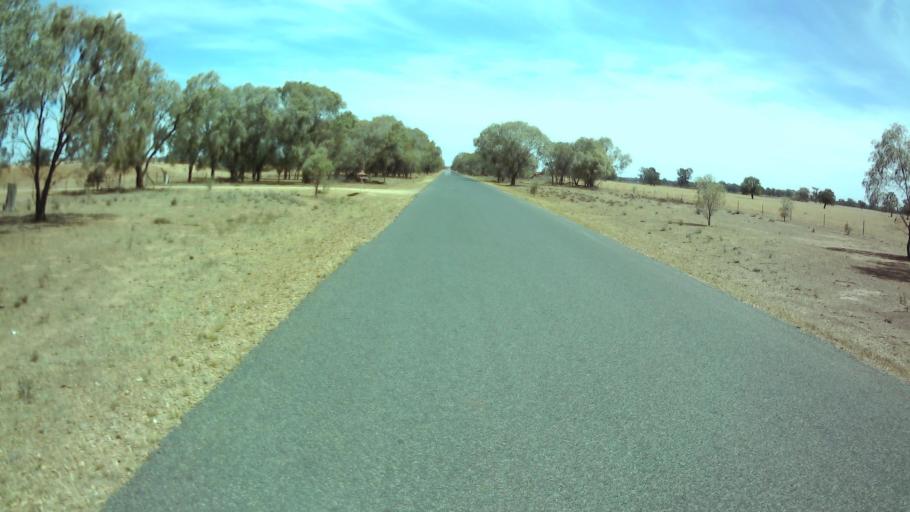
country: AU
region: New South Wales
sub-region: Weddin
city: Grenfell
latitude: -33.8708
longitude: 147.7448
